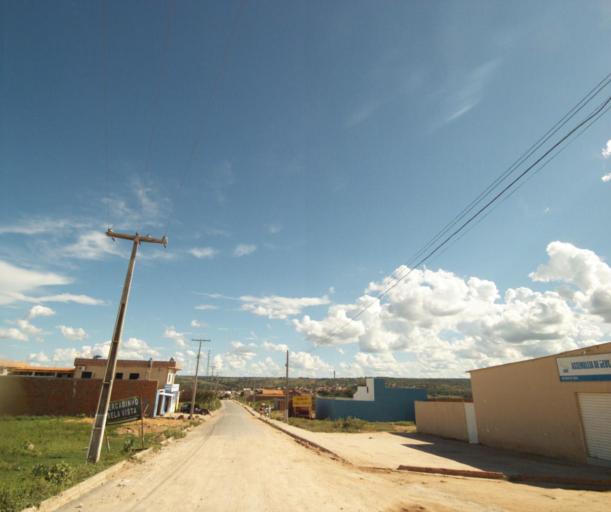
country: BR
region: Bahia
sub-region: Correntina
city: Correntina
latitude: -13.3318
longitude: -44.6388
